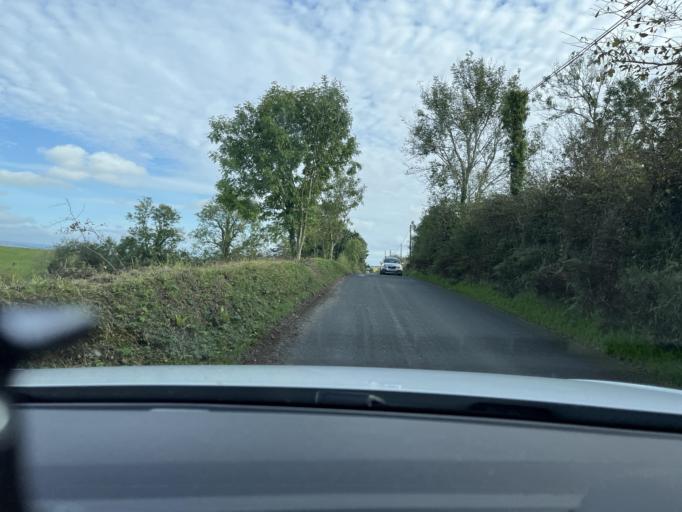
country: IE
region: Connaught
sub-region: Sligo
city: Ballymote
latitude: 54.0826
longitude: -8.4274
